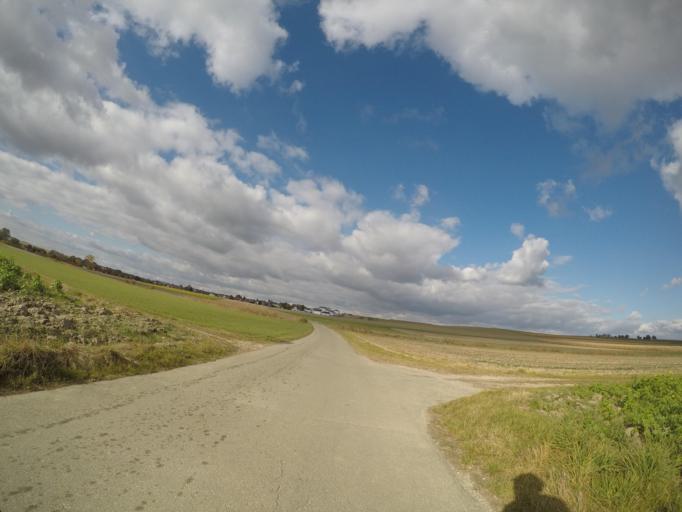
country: DE
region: Baden-Wuerttemberg
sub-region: Tuebingen Region
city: Unterstadion
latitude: 48.1976
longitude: 9.7004
